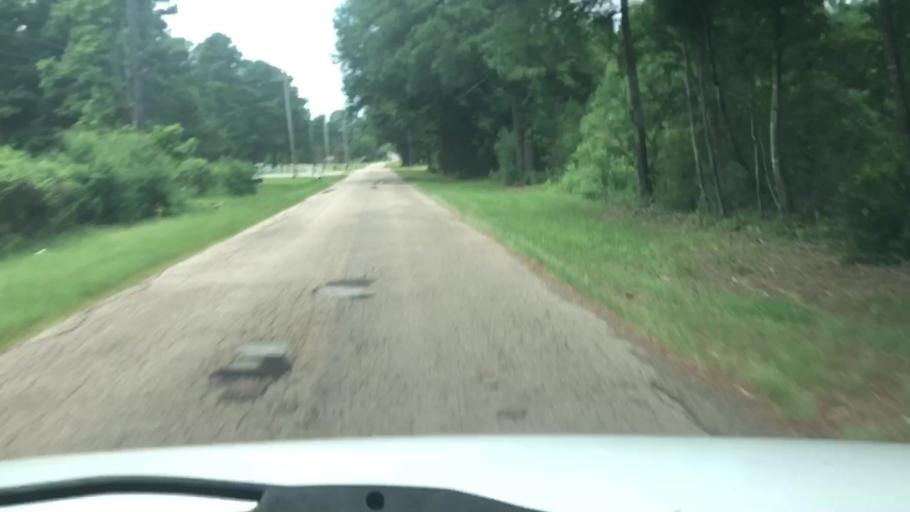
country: US
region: Texas
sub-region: Bowie County
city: Wake Village
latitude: 33.3889
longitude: -94.0813
